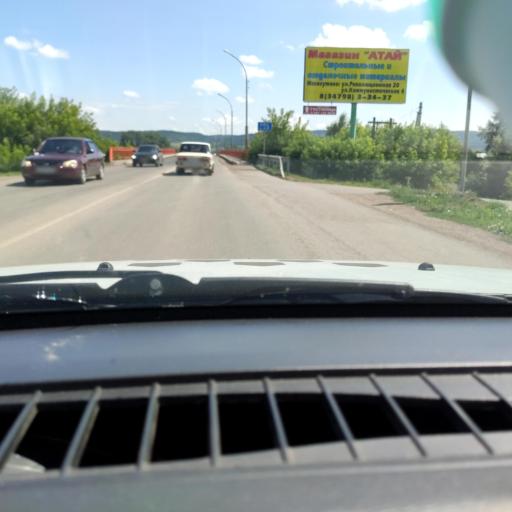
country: RU
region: Bashkortostan
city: Mesyagutovo
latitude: 55.5316
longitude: 58.2514
